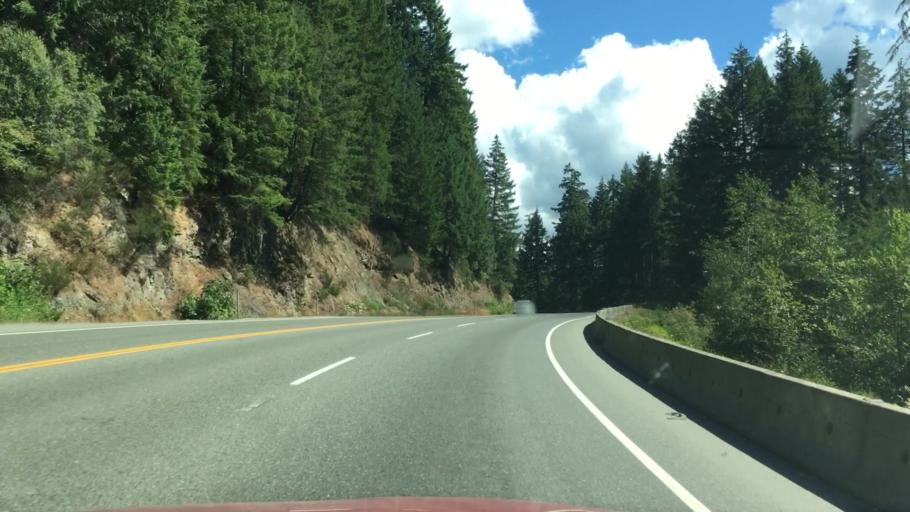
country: CA
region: British Columbia
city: Port Alberni
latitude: 49.2661
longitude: -124.7318
